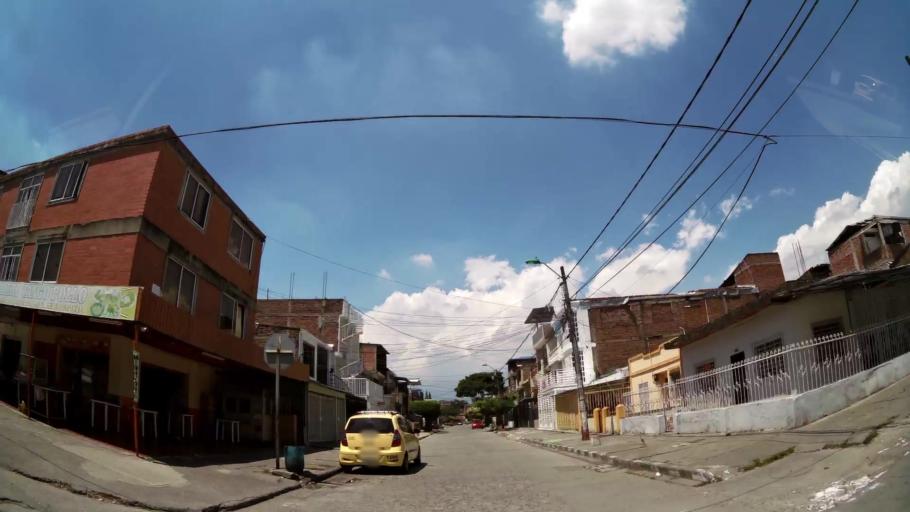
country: CO
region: Valle del Cauca
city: Cali
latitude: 3.4398
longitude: -76.4987
